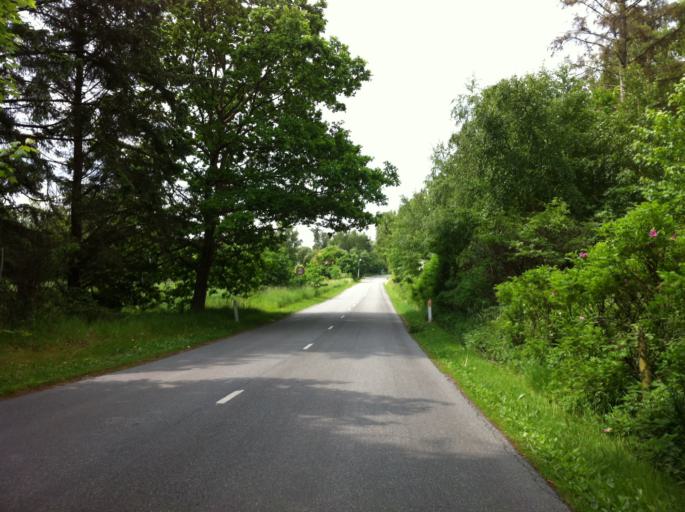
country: DK
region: Capital Region
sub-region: Gribskov Kommune
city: Helsinge
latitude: 56.1092
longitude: 12.1971
